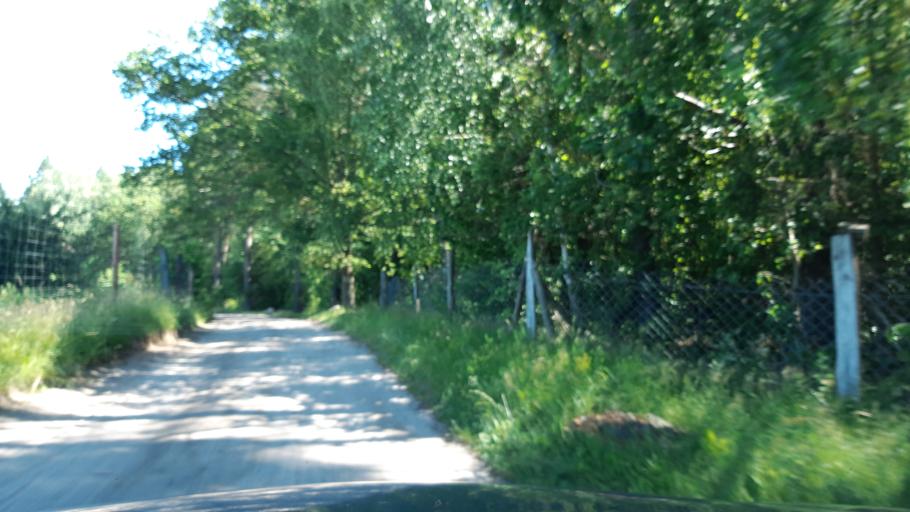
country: PL
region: Warmian-Masurian Voivodeship
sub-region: Powiat piski
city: Ruciane-Nida
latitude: 53.7102
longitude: 21.4883
